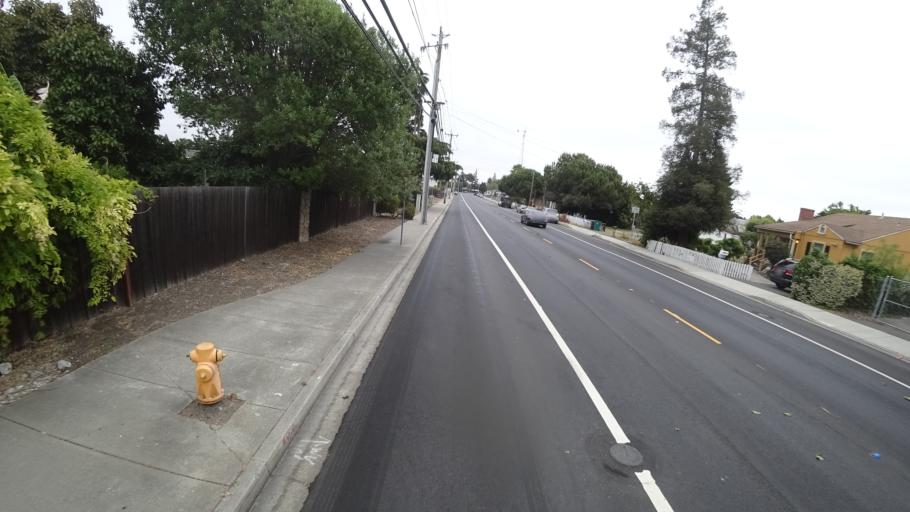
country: US
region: California
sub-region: Alameda County
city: Hayward
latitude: 37.6236
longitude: -122.0651
